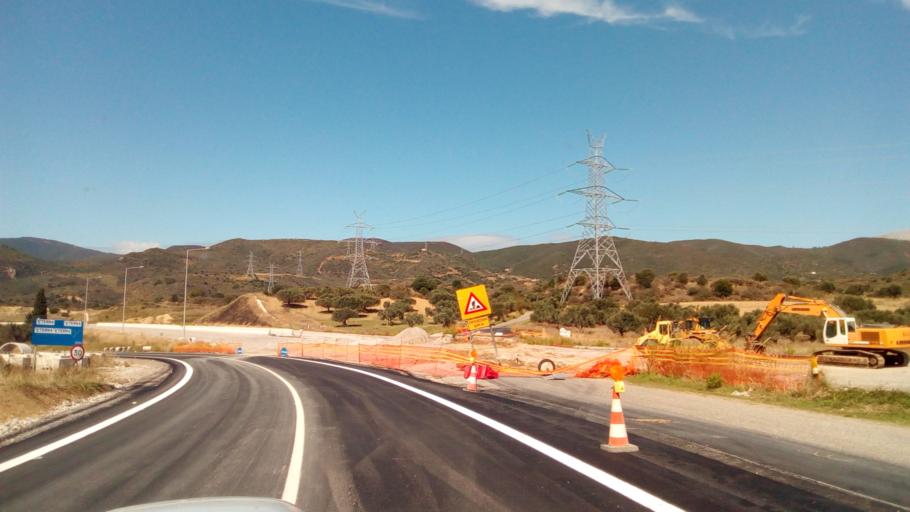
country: GR
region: West Greece
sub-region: Nomos Aitolias kai Akarnanias
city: Antirrio
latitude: 38.3450
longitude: 21.7552
